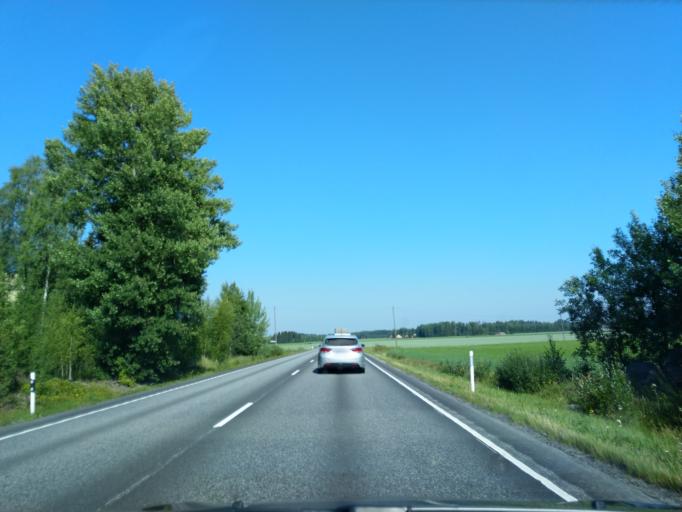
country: FI
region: Varsinais-Suomi
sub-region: Loimaa
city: Alastaro
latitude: 61.0870
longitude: 22.8901
